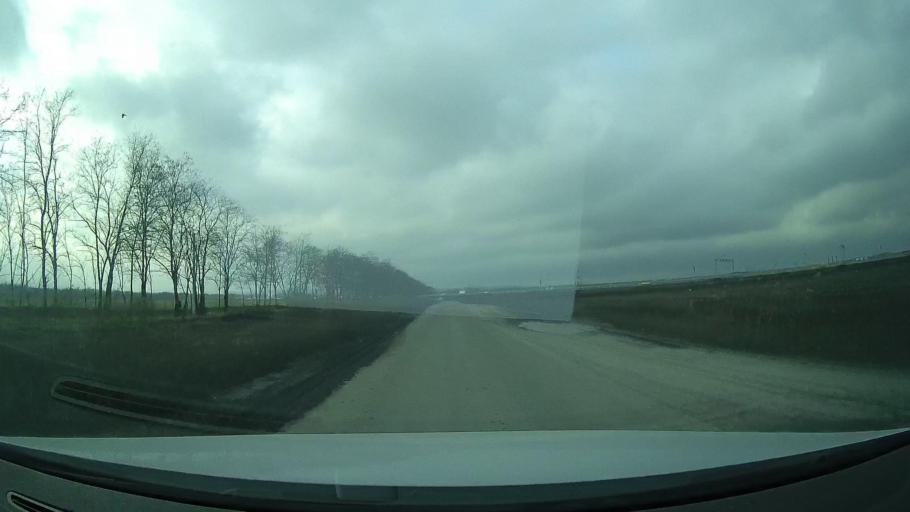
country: RU
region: Rostov
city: Grushevskaya
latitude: 47.4797
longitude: 39.9266
